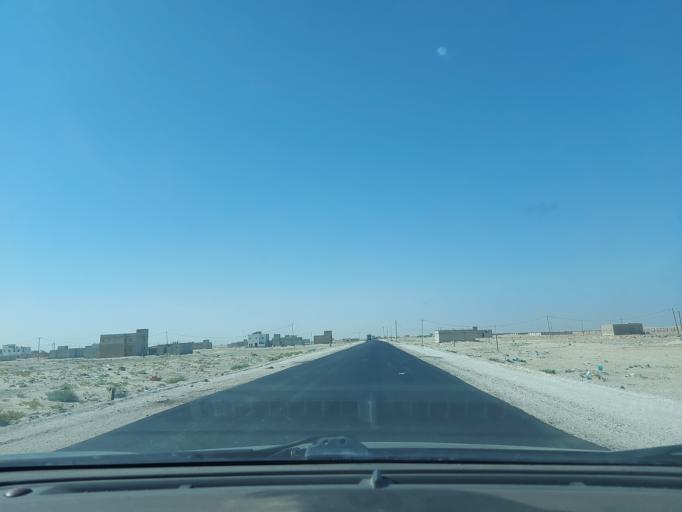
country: MR
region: Nouakchott
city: Nouakchott
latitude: 17.9973
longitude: -15.9882
